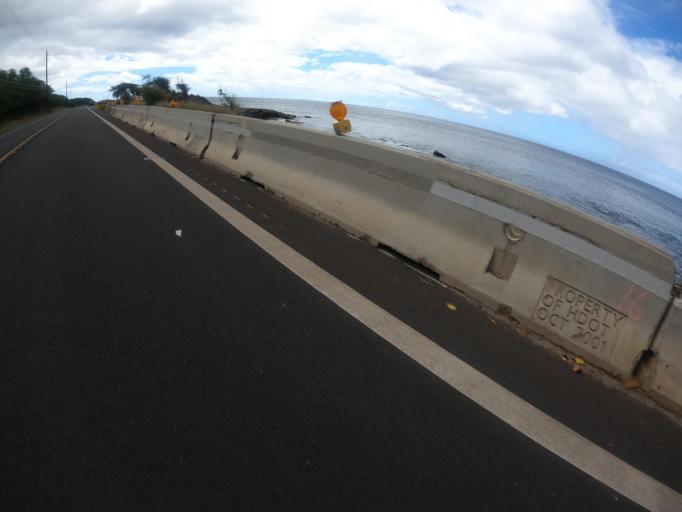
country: US
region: Hawaii
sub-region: Honolulu County
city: Makaha Valley
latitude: 21.5045
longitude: -158.2294
